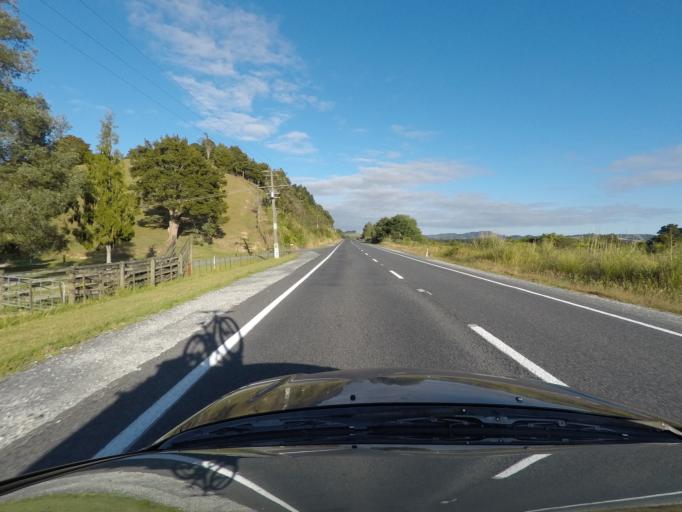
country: NZ
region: Northland
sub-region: Far North District
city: Kawakawa
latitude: -35.5313
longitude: 174.2270
